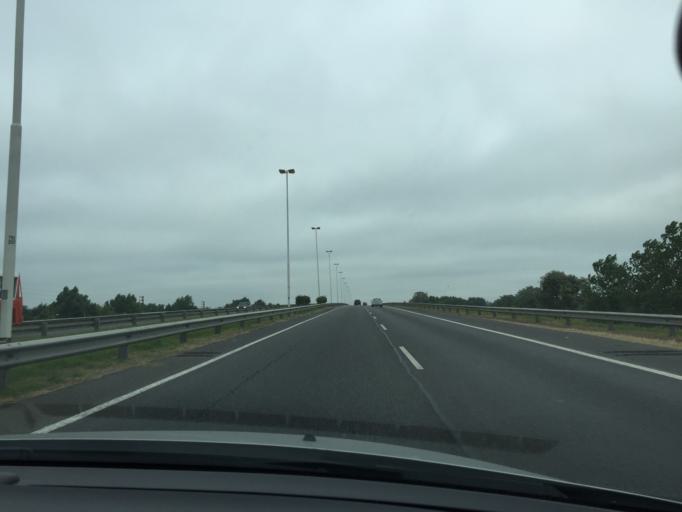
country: AR
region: Buenos Aires
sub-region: Partido de Ezeiza
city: Ezeiza
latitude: -34.8478
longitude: -58.5401
